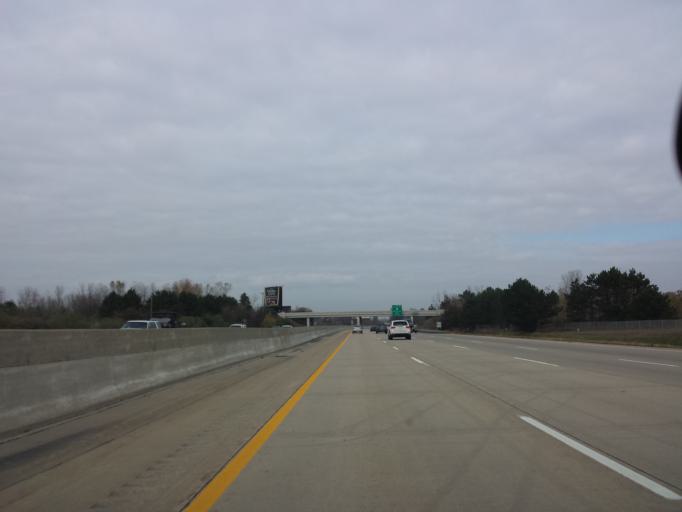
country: US
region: Michigan
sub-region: Genesee County
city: Clio
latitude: 43.1606
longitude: -83.7671
